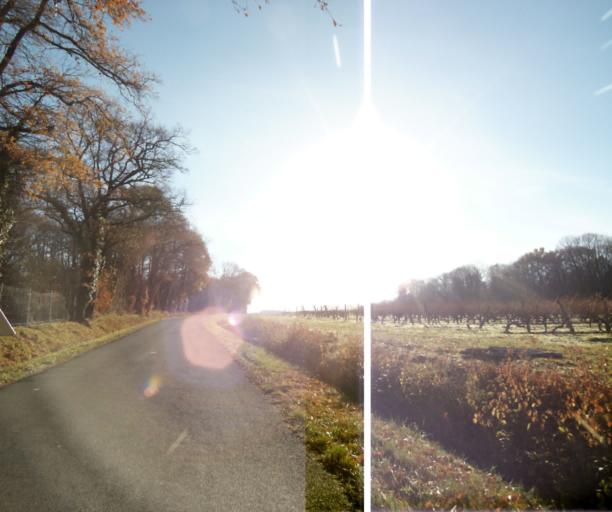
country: FR
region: Poitou-Charentes
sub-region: Departement de la Charente-Maritime
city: Cherac
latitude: 45.7377
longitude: -0.4362
